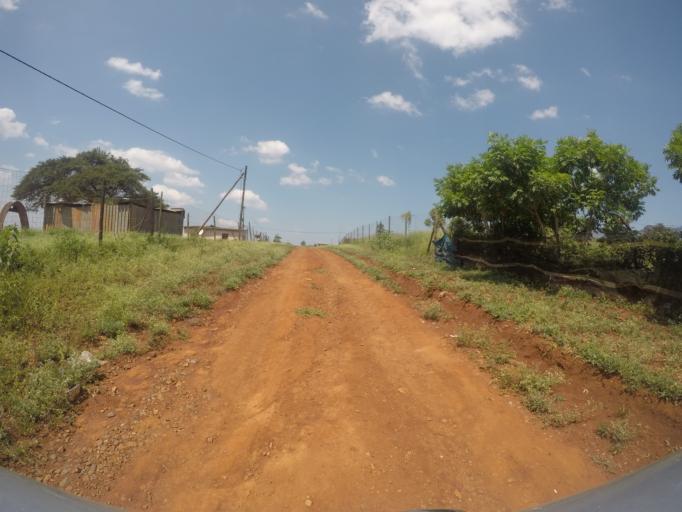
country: ZA
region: KwaZulu-Natal
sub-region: uThungulu District Municipality
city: Empangeni
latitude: -28.5938
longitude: 31.7386
